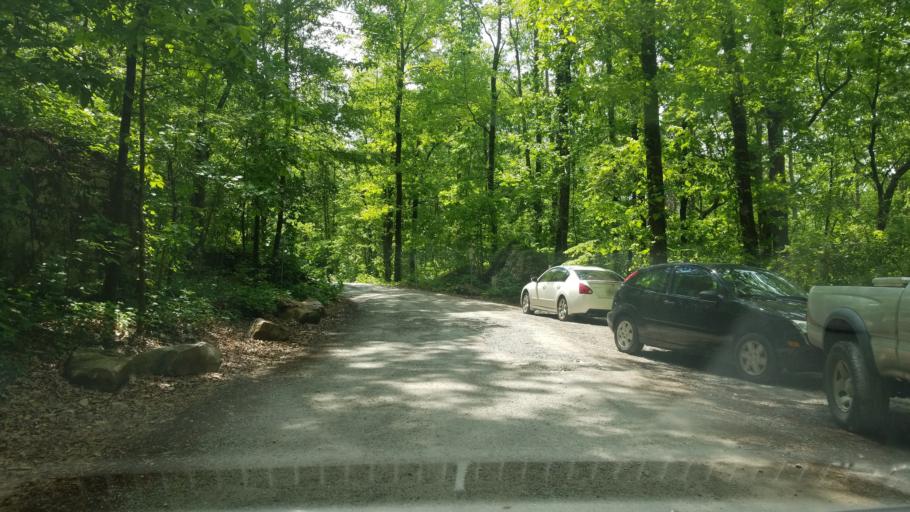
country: US
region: Tennessee
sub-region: Hamilton County
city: Falling Water
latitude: 35.2364
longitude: -85.2338
